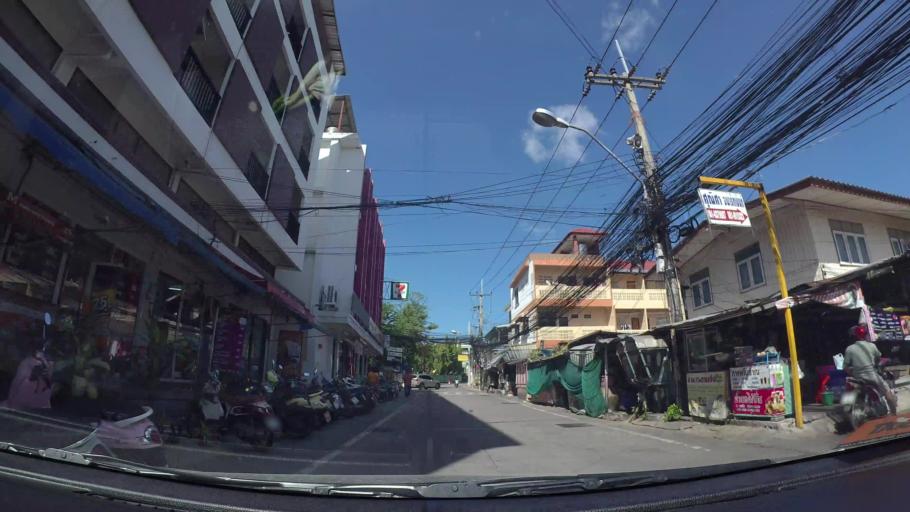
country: TH
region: Chon Buri
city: Phatthaya
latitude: 12.9394
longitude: 100.9000
